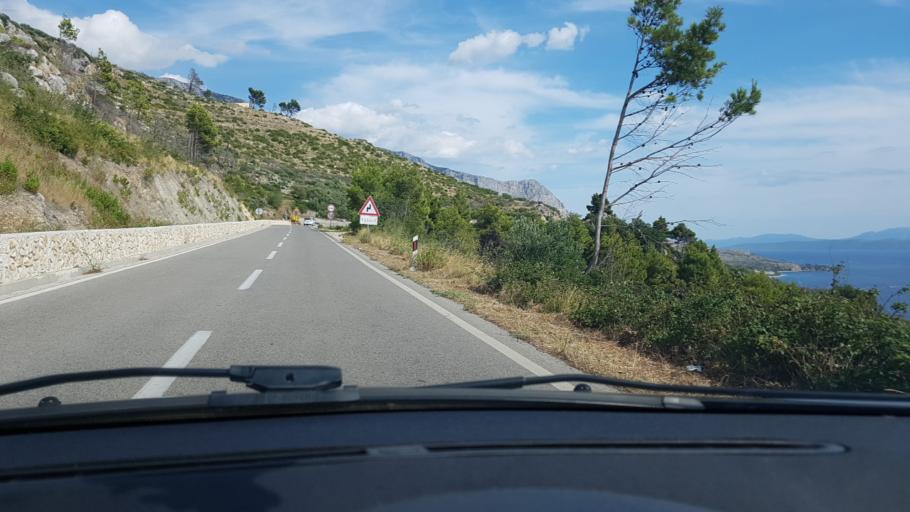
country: HR
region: Splitsko-Dalmatinska
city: Tucepi
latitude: 43.2807
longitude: 17.0446
